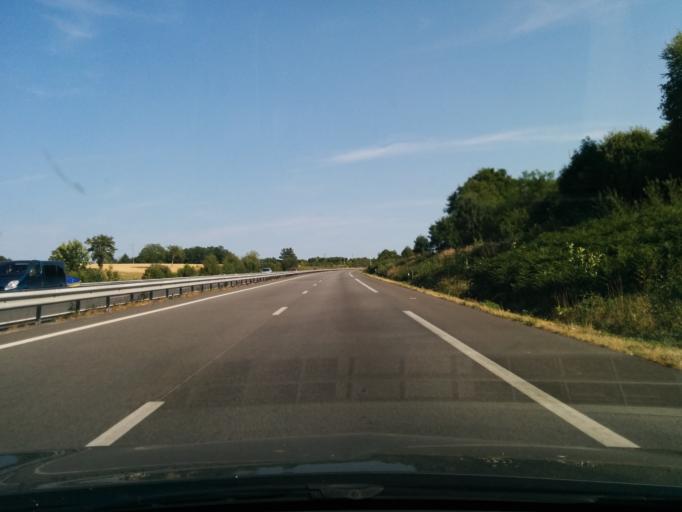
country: FR
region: Limousin
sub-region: Departement de la Haute-Vienne
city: Vicq-sur-Breuilh
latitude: 45.6604
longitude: 1.3966
